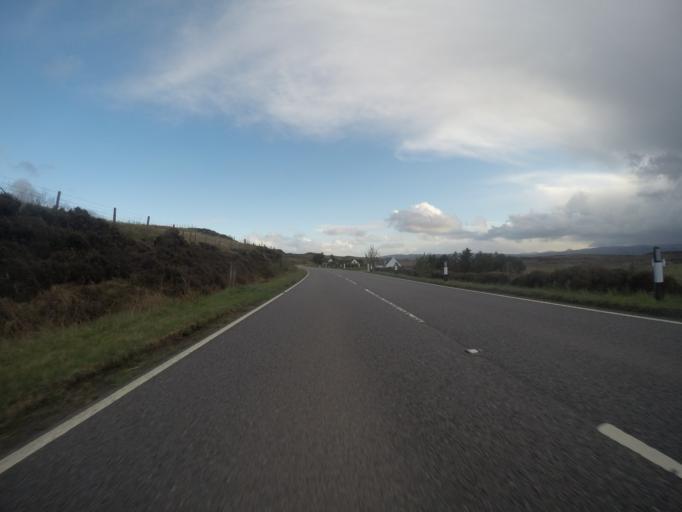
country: GB
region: Scotland
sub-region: Highland
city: Portree
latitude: 57.5625
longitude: -6.3644
